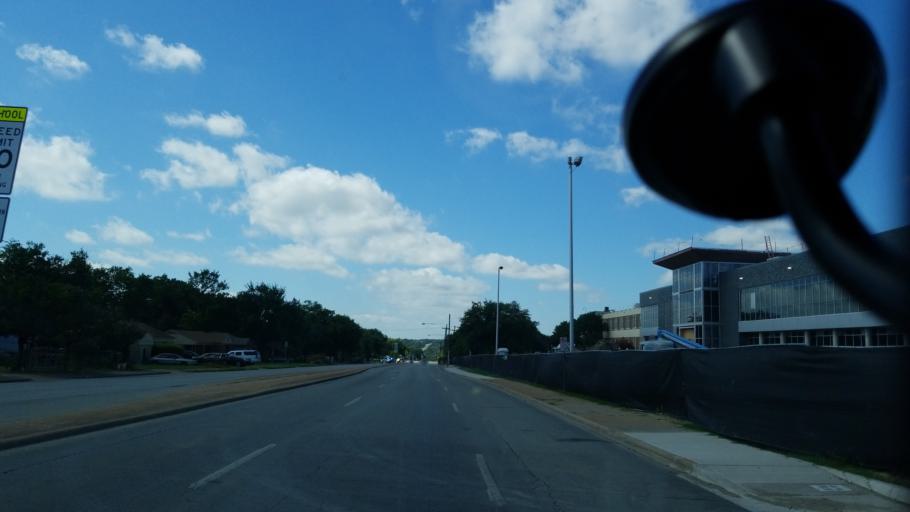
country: US
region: Texas
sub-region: Dallas County
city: Cockrell Hill
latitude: 32.7004
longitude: -96.8147
